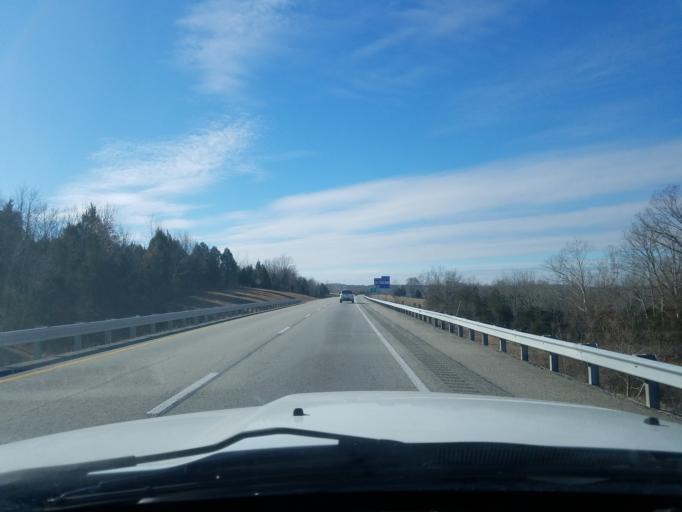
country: US
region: Kentucky
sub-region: Grayson County
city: Leitchfield
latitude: 37.4691
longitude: -86.2688
